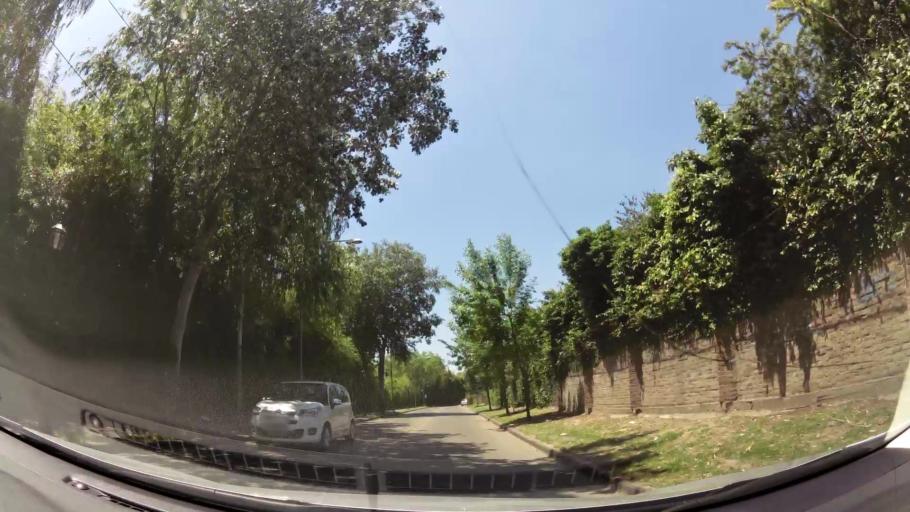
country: AR
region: Buenos Aires
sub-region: Partido de Tigre
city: Tigre
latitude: -34.4294
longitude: -58.5960
